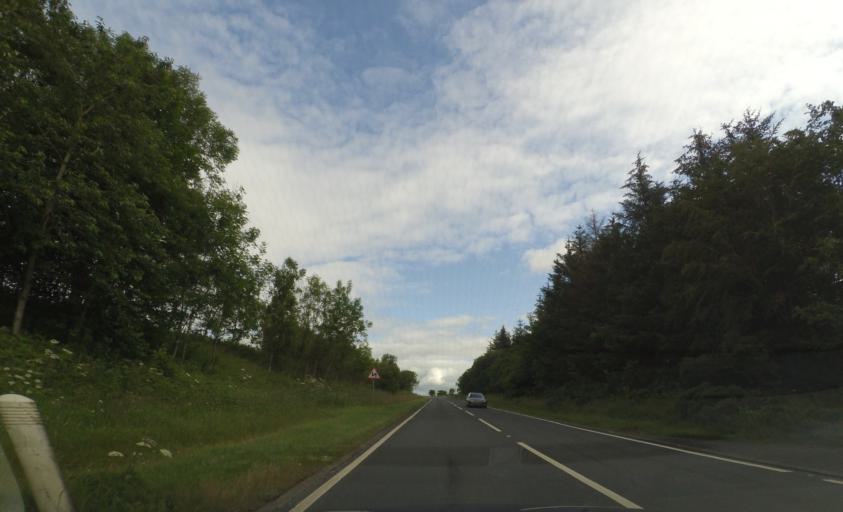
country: GB
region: Scotland
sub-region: The Scottish Borders
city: Hawick
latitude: 55.4568
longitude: -2.7797
